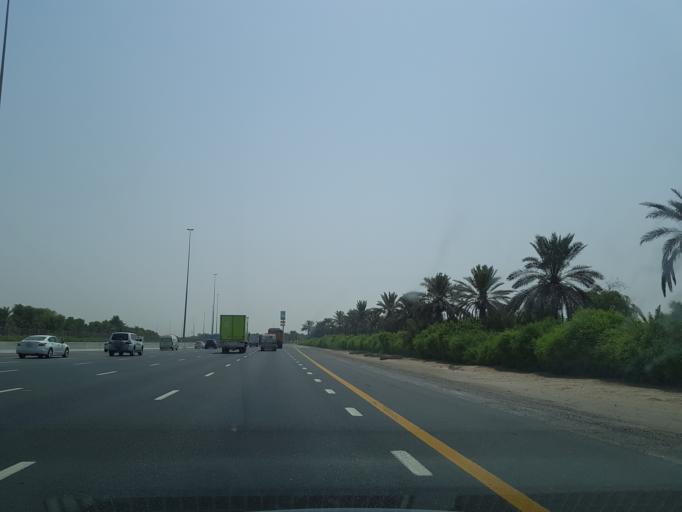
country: AE
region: Dubai
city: Dubai
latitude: 25.0595
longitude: 55.2819
